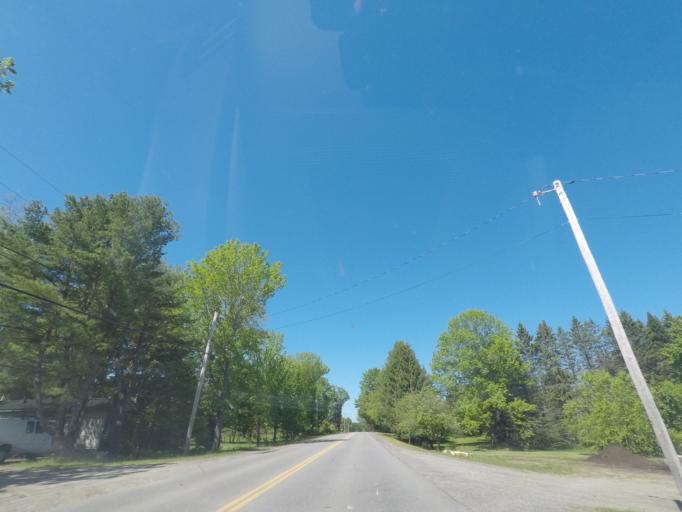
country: US
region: Maine
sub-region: Kennebec County
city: Gardiner
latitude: 44.2314
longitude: -69.7996
